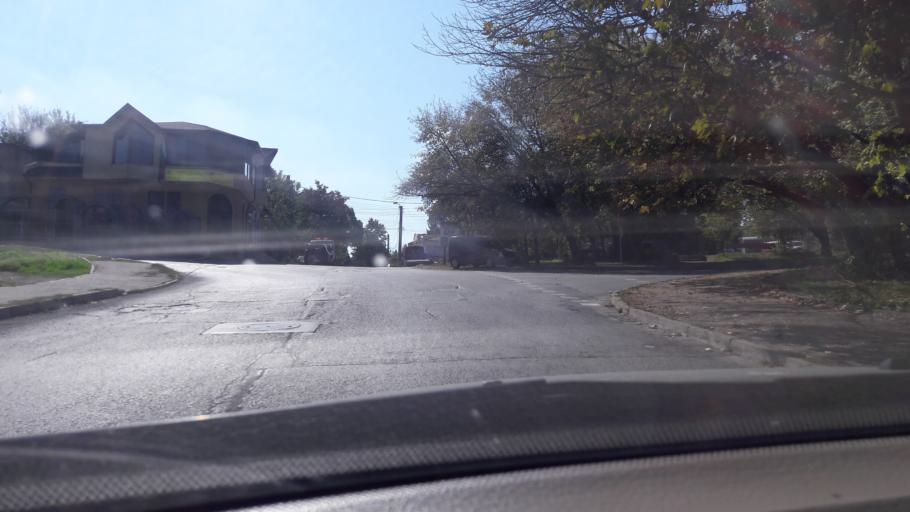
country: BG
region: Razgrad
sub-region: Obshtina Razgrad
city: Razgrad
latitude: 43.5254
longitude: 26.5150
